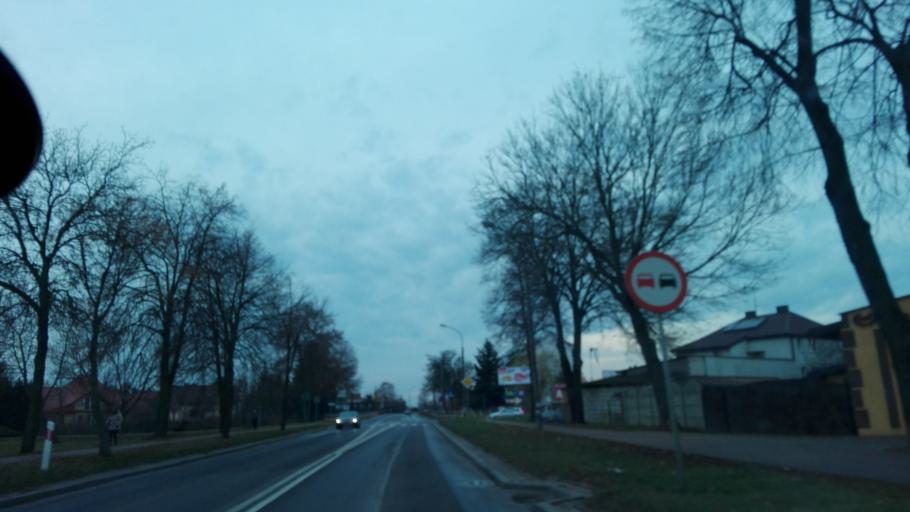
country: PL
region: Lublin Voivodeship
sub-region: Powiat radzynski
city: Radzyn Podlaski
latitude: 51.7728
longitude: 22.6065
